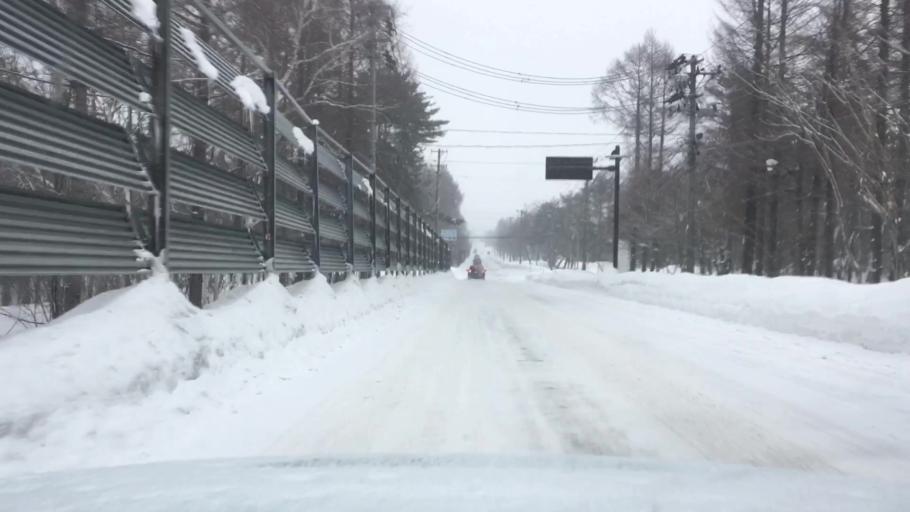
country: JP
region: Akita
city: Hanawa
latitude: 40.0059
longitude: 140.9727
